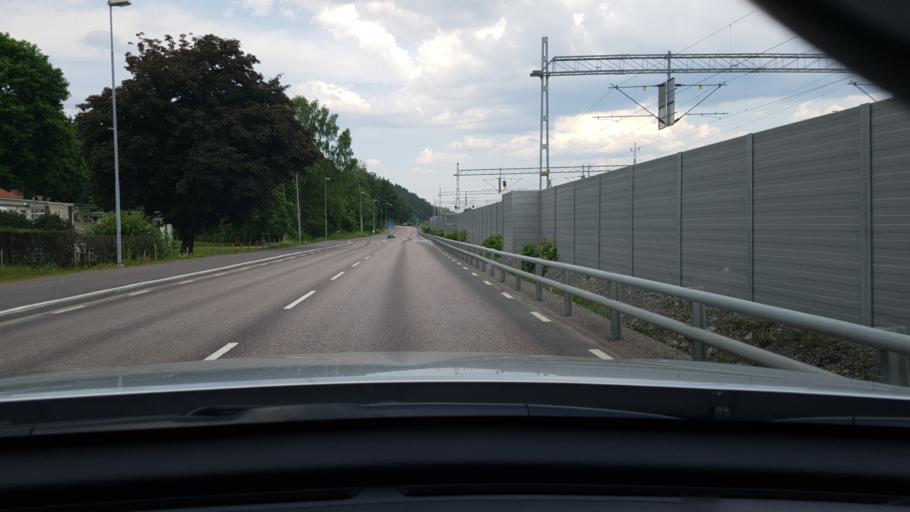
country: SE
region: Vaestra Goetaland
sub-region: Lerums Kommun
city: Stenkullen
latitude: 57.7971
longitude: 12.3229
